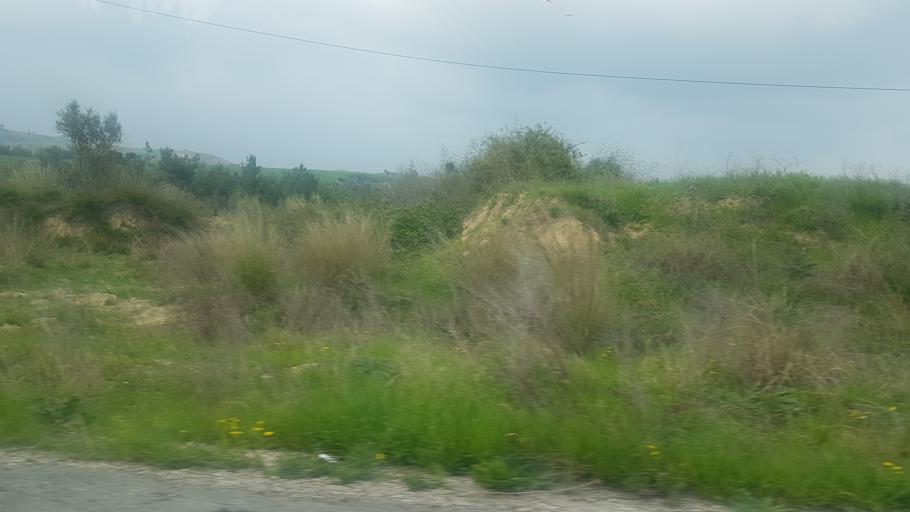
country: TR
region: Adana
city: Seyhan
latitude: 37.0437
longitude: 35.1836
